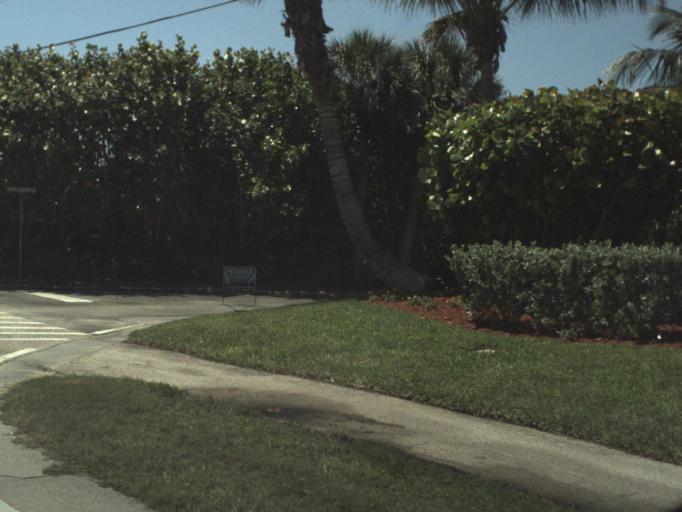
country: US
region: Florida
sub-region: Brevard County
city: Melbourne Beach
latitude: 28.0385
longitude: -80.5439
